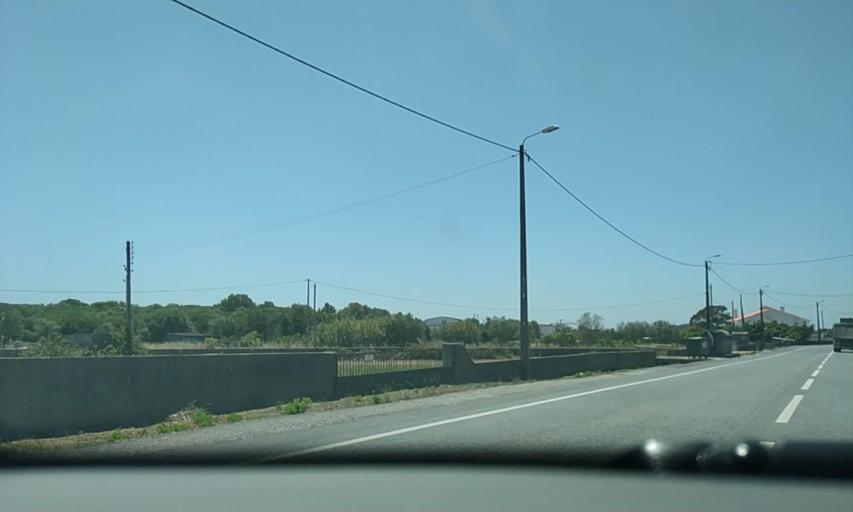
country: PT
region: Lisbon
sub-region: Sintra
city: Almargem
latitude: 38.8773
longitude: -9.2699
